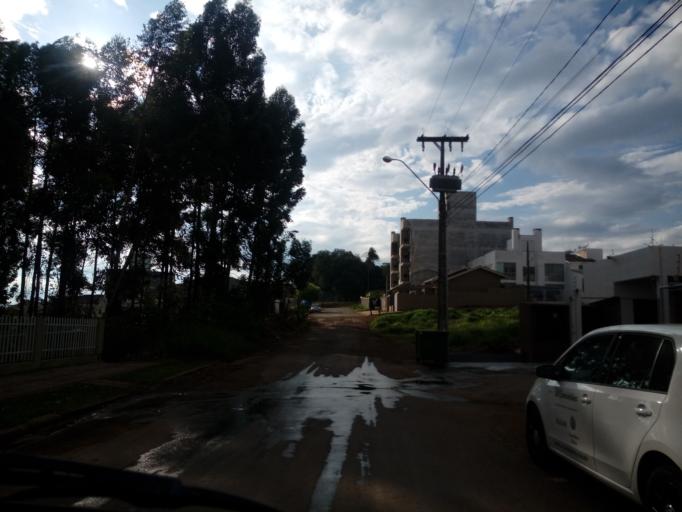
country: BR
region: Santa Catarina
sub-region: Chapeco
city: Chapeco
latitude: -27.0891
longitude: -52.5948
